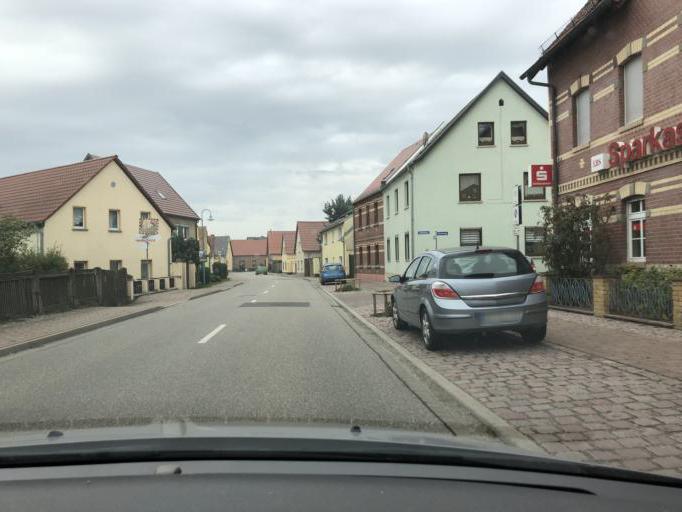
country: DE
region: Saxony-Anhalt
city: Uichteritz
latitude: 51.2075
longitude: 11.9273
